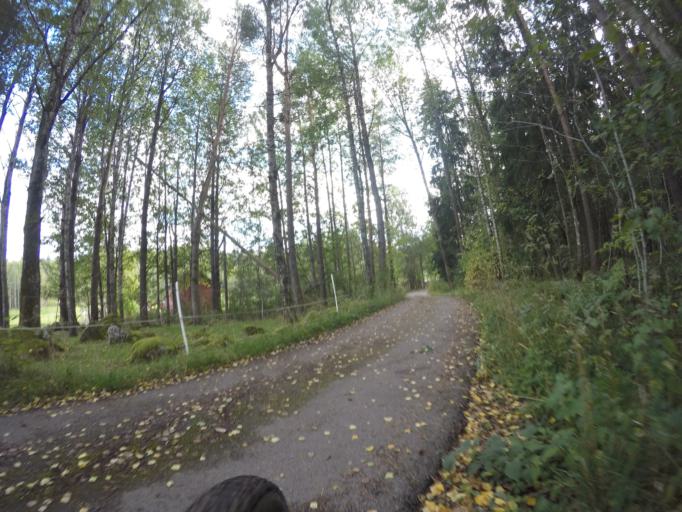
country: SE
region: Vaestmanland
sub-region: Kopings Kommun
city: Koping
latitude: 59.5100
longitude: 16.0207
